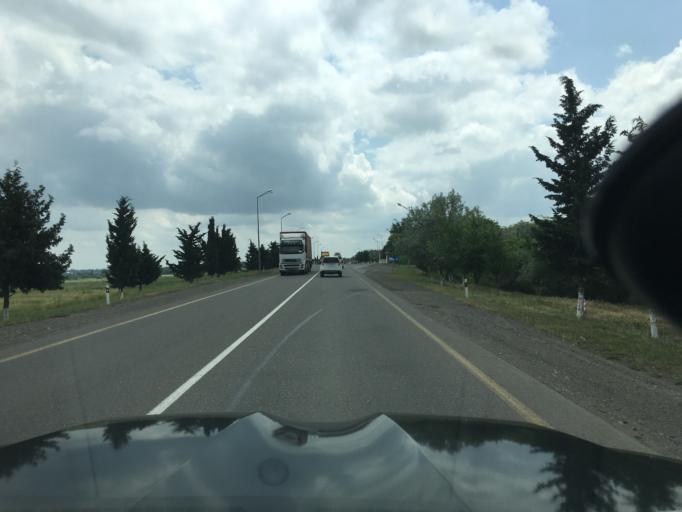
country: AZ
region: Tovuz
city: Qaraxanli
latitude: 41.0498
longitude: 45.5707
